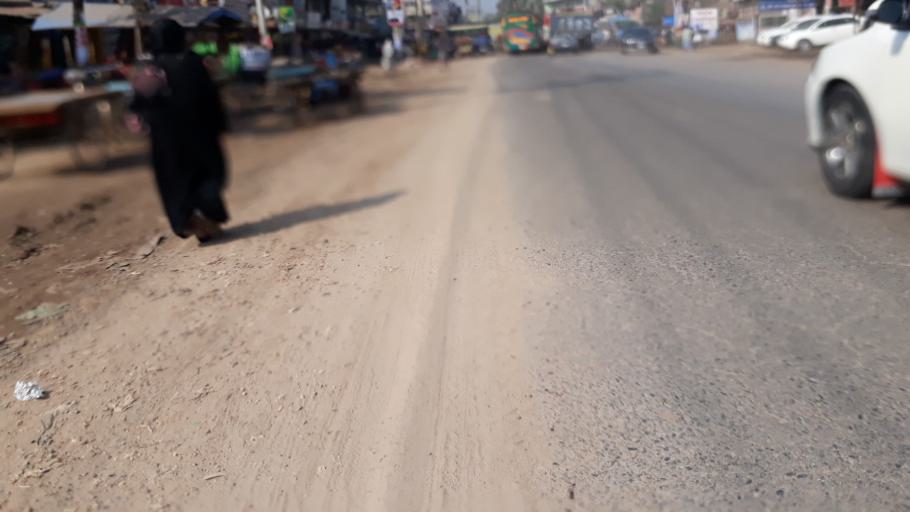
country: BD
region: Dhaka
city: Tungi
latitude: 23.9125
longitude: 90.3194
